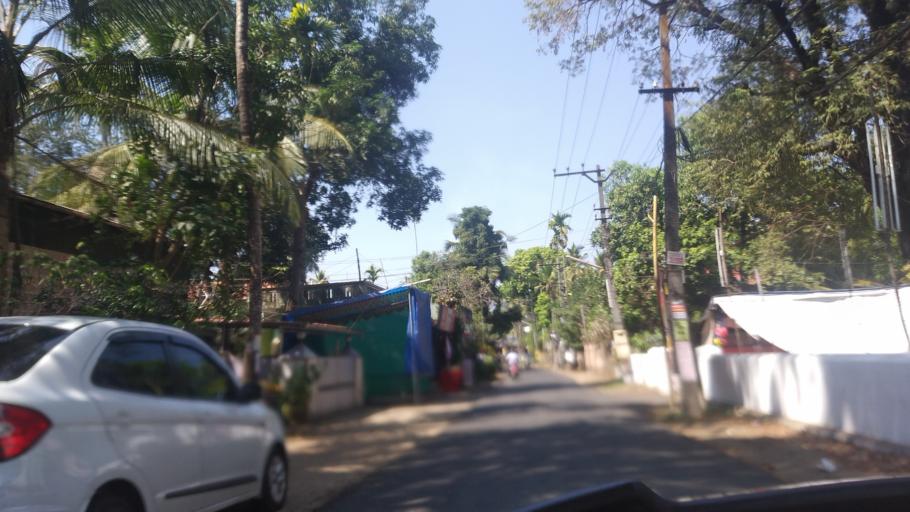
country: IN
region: Kerala
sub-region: Ernakulam
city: Elur
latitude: 10.1328
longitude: 76.2276
